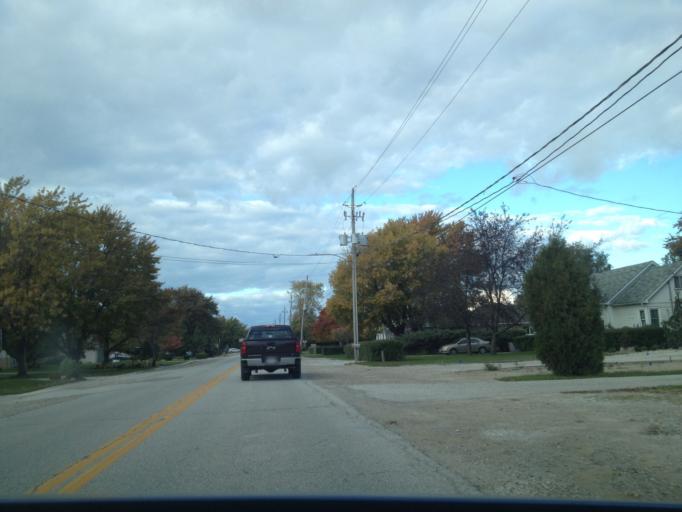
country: US
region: Michigan
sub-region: Wayne County
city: Grosse Pointe Farms
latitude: 42.2856
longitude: -82.7122
